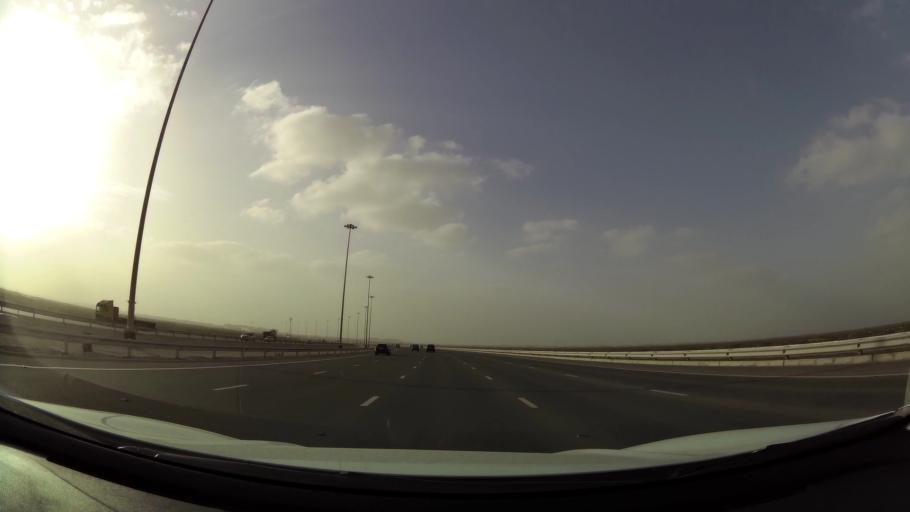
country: AE
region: Abu Dhabi
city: Abu Dhabi
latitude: 24.5438
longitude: 54.4805
